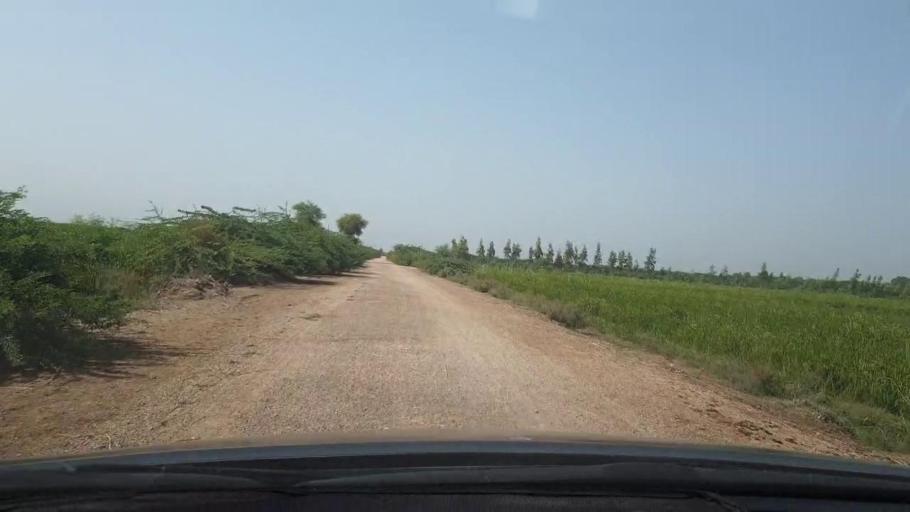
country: PK
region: Sindh
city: Tando Bago
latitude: 24.7198
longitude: 69.0950
